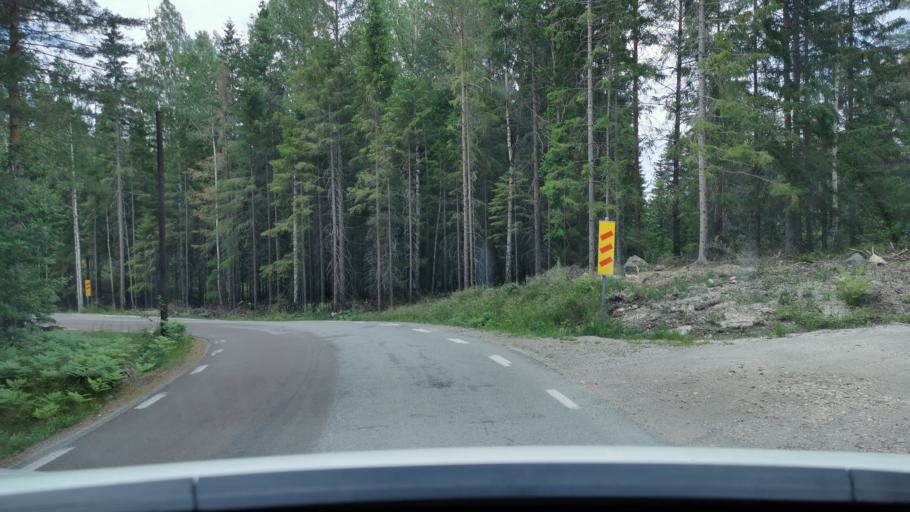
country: SE
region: Vaestra Goetaland
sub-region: Bengtsfors Kommun
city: Dals Langed
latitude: 58.8344
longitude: 12.4119
